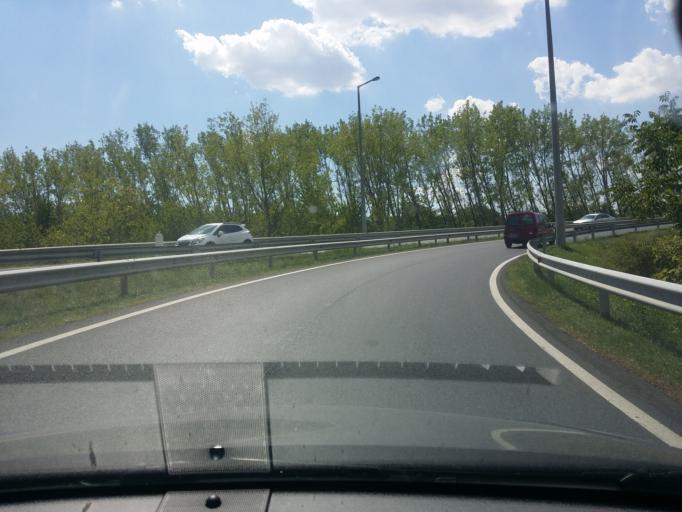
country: HU
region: Pest
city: Budaors
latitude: 47.4513
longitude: 18.9508
